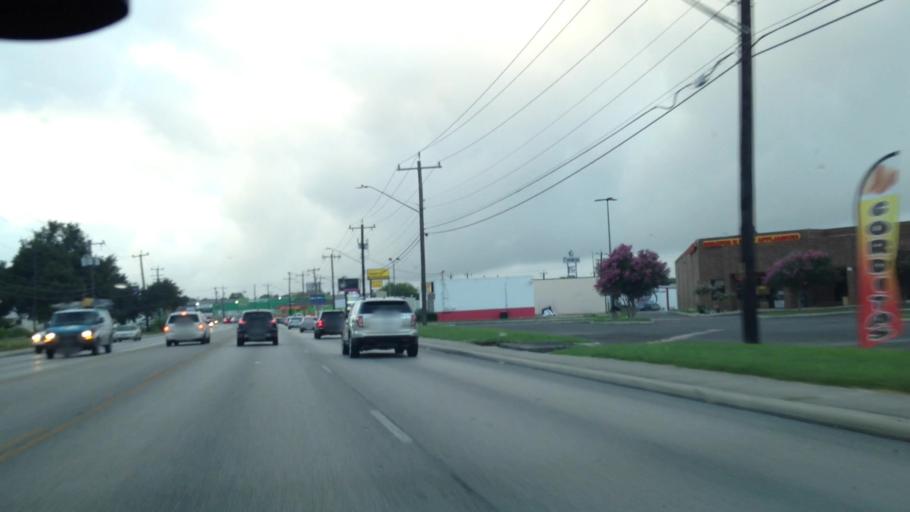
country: US
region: Texas
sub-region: Bexar County
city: Windcrest
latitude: 29.5474
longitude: -98.4096
